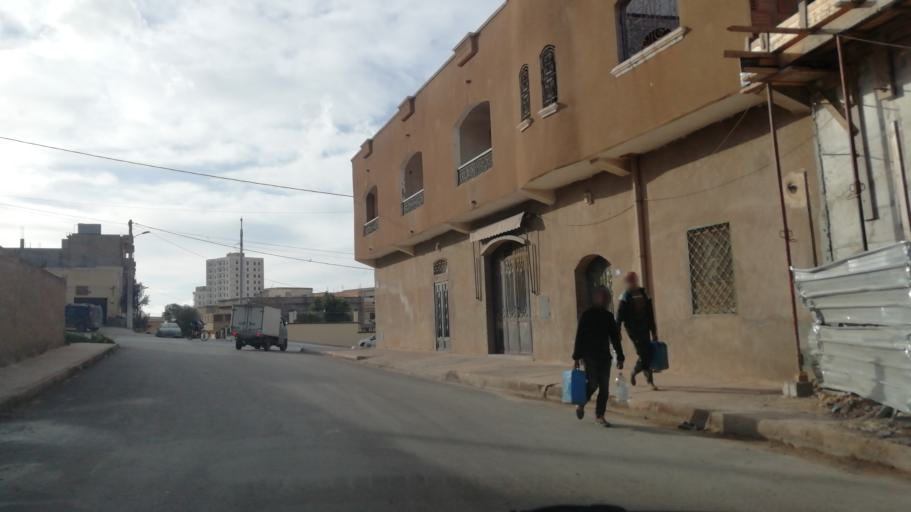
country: DZ
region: Oran
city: Bir el Djir
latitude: 35.7324
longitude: -0.5723
